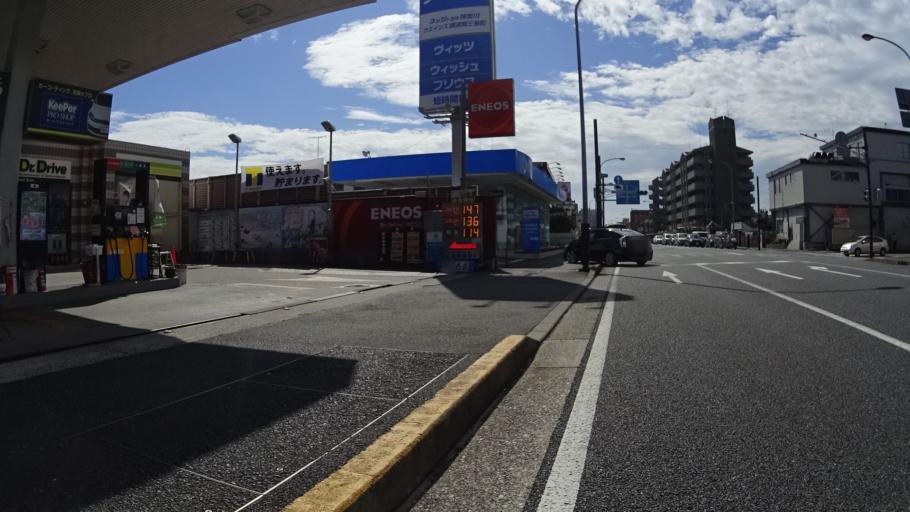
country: JP
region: Kanagawa
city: Yokosuka
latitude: 35.2654
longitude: 139.6896
